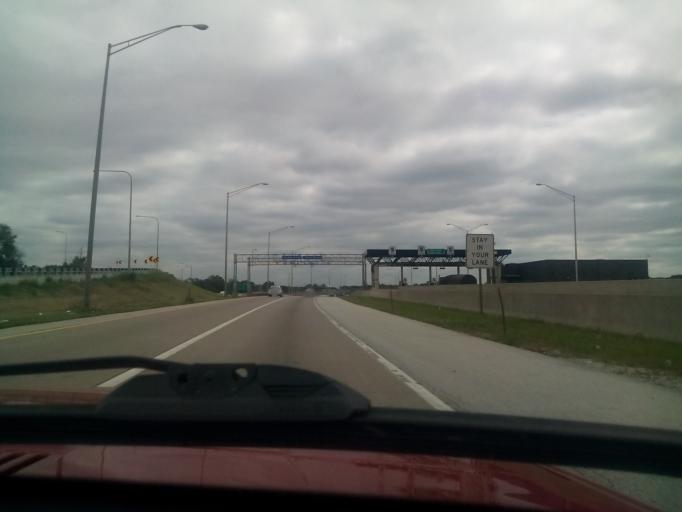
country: US
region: Illinois
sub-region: Cook County
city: University Park
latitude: 41.5819
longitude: -87.6821
